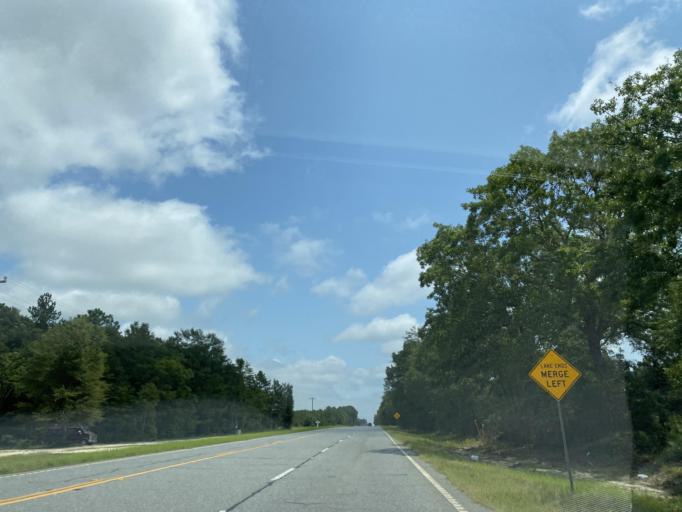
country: US
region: Georgia
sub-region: Telfair County
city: McRae
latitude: 32.0882
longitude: -82.8710
